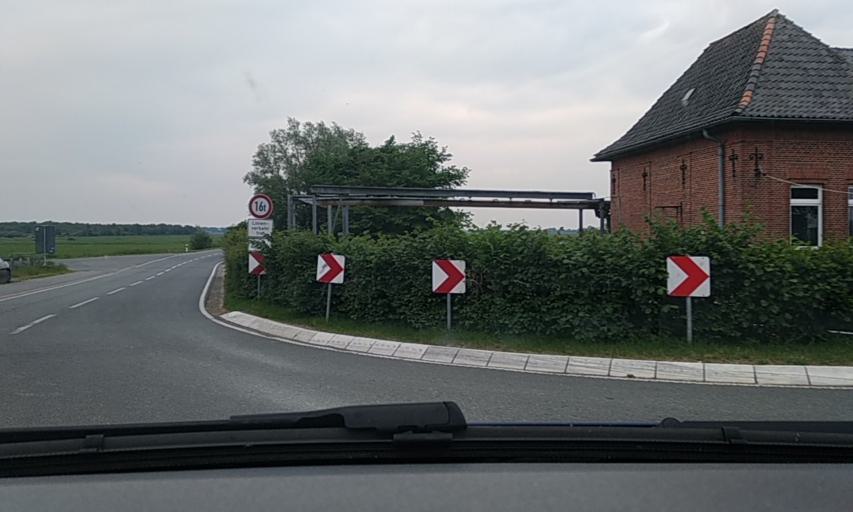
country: DE
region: Schleswig-Holstein
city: Christiansholm
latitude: 54.3215
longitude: 9.3862
